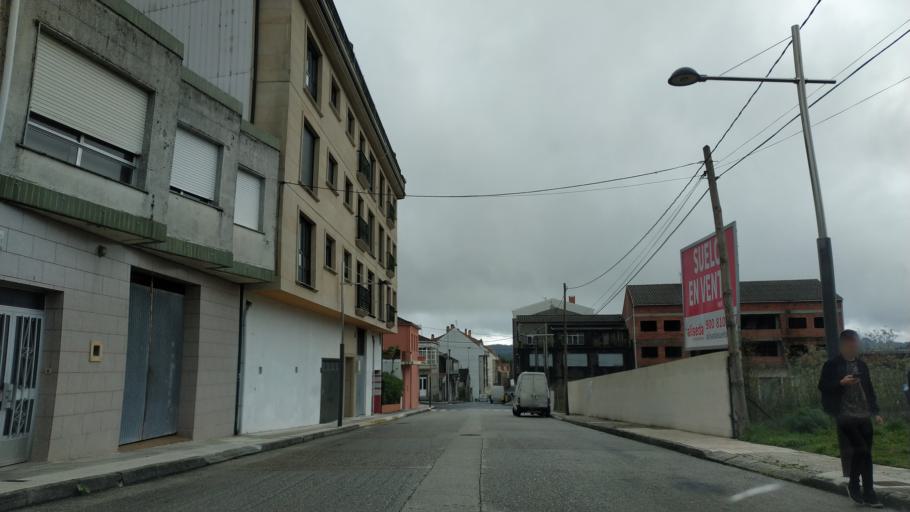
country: ES
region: Galicia
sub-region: Provincia da Coruna
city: Negreira
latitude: 42.9106
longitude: -8.7400
